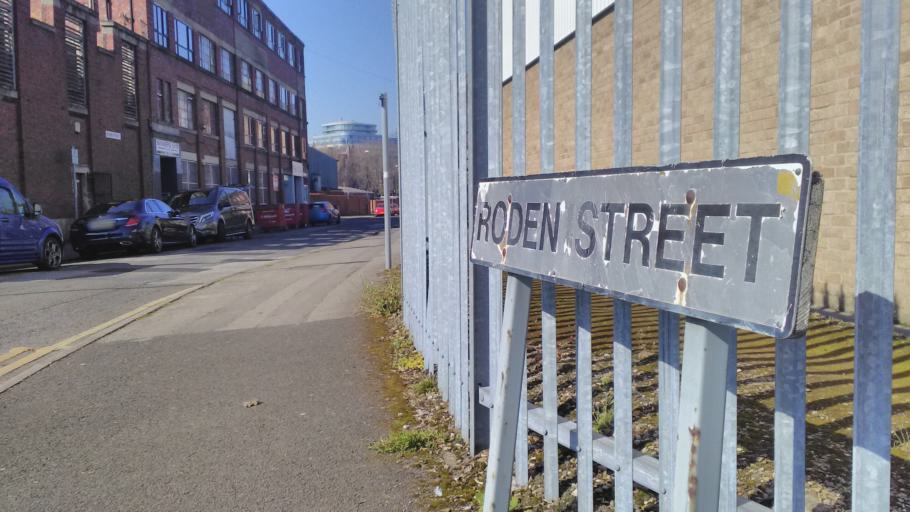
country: GB
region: England
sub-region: Nottingham
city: Nottingham
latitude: 52.9562
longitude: -1.1351
